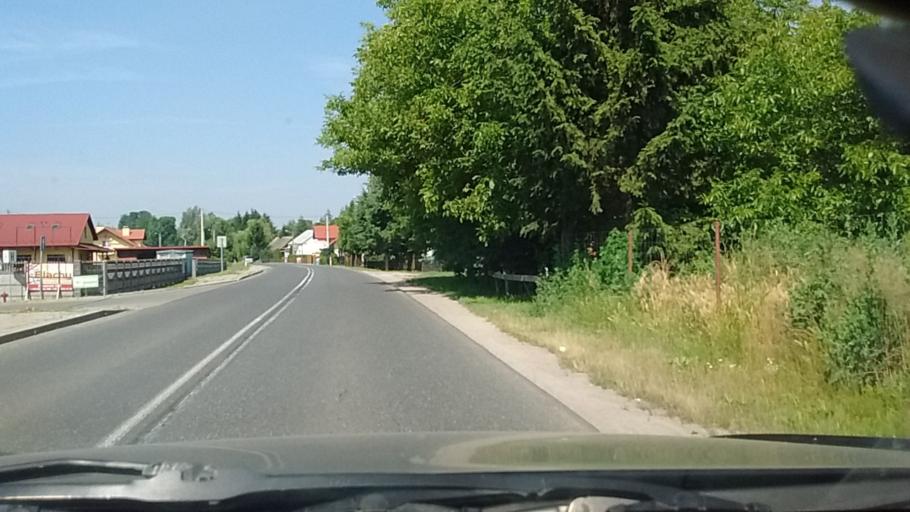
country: PL
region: Subcarpathian Voivodeship
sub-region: Powiat lancucki
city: Sonina
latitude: 50.0564
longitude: 22.2724
